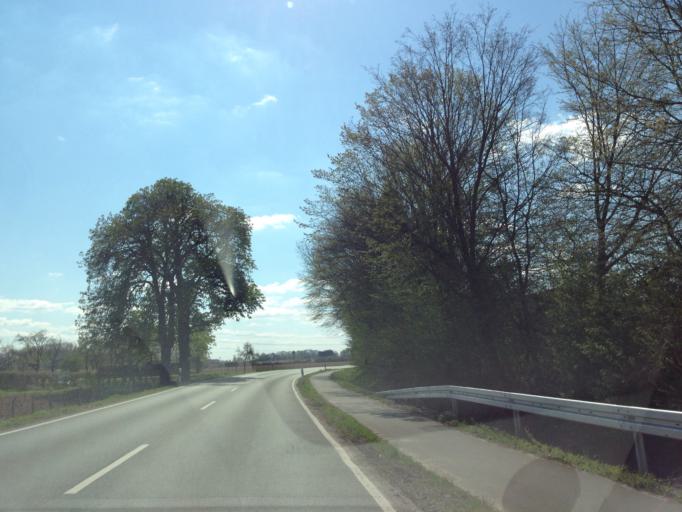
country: DE
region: North Rhine-Westphalia
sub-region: Regierungsbezirk Munster
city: Muenster
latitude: 51.9106
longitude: 7.5920
